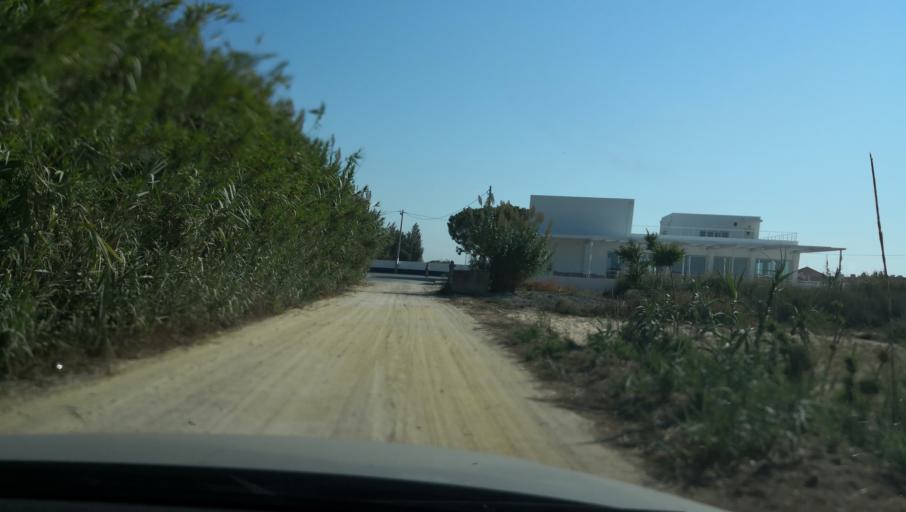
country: PT
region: Setubal
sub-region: Setubal
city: Setubal
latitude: 38.3824
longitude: -8.7885
